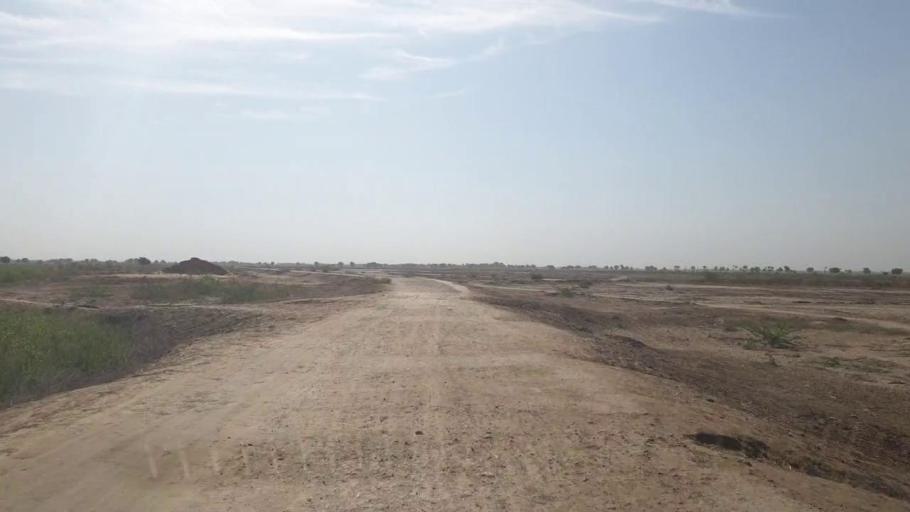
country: PK
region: Sindh
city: Umarkot
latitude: 25.2867
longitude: 69.6541
